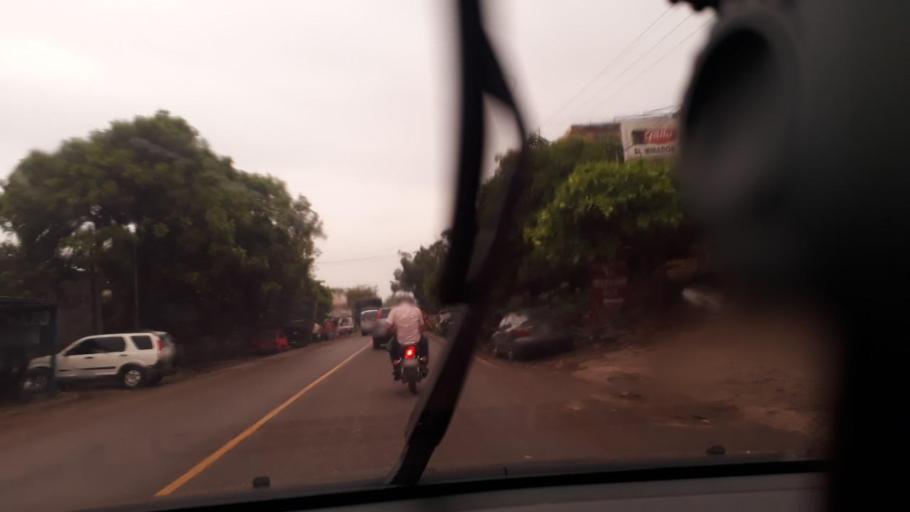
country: GT
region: Jutiapa
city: Asuncion Mita
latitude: 14.3283
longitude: -89.7116
